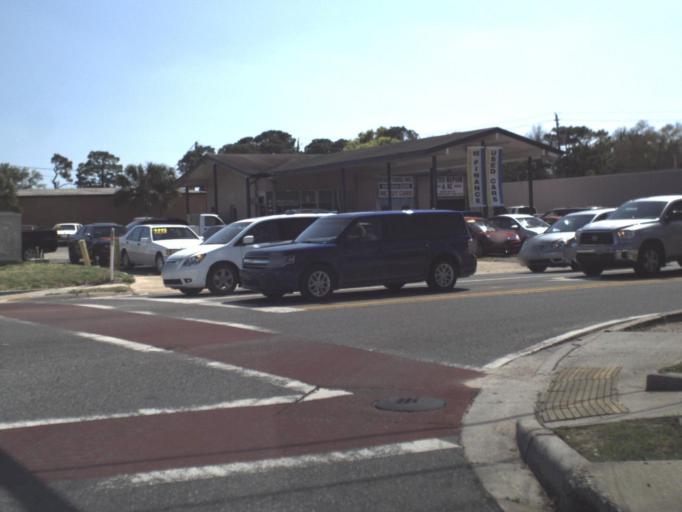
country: US
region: Florida
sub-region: Okaloosa County
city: Fort Walton Beach
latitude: 30.4127
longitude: -86.6131
